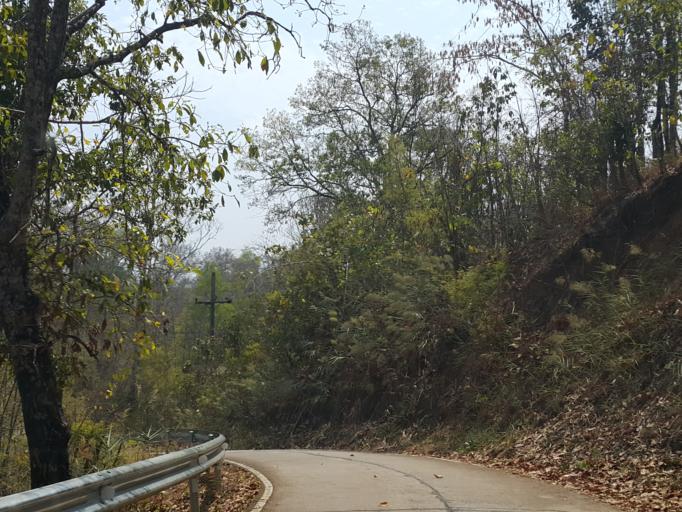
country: TH
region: Lampang
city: Mueang Pan
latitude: 18.8155
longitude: 99.4735
